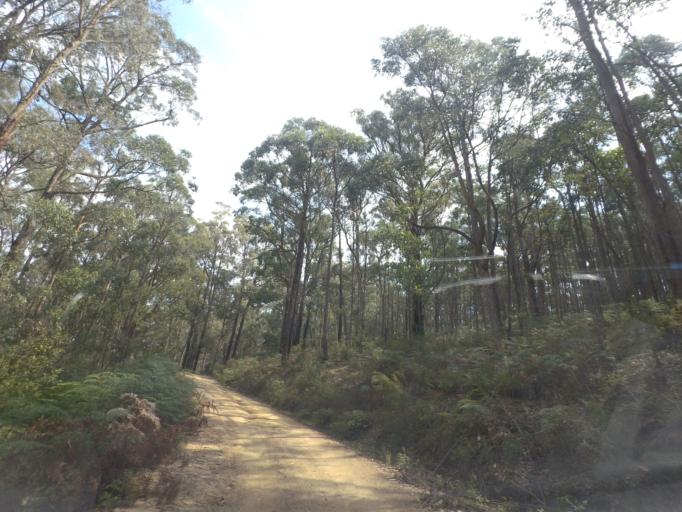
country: AU
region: Victoria
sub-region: Moorabool
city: Bacchus Marsh
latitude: -37.4634
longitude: 144.3766
